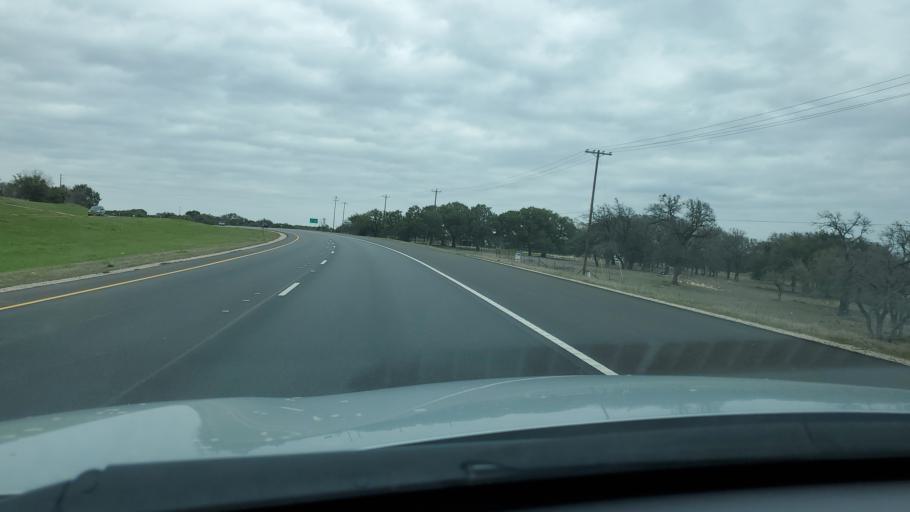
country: US
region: Texas
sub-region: Williamson County
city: Florence
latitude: 30.9424
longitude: -97.7853
